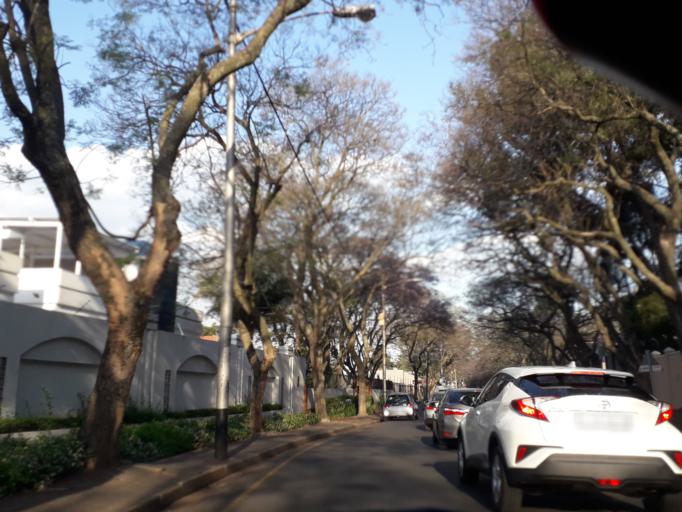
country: ZA
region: Gauteng
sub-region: City of Johannesburg Metropolitan Municipality
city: Johannesburg
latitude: -26.1702
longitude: 28.0620
